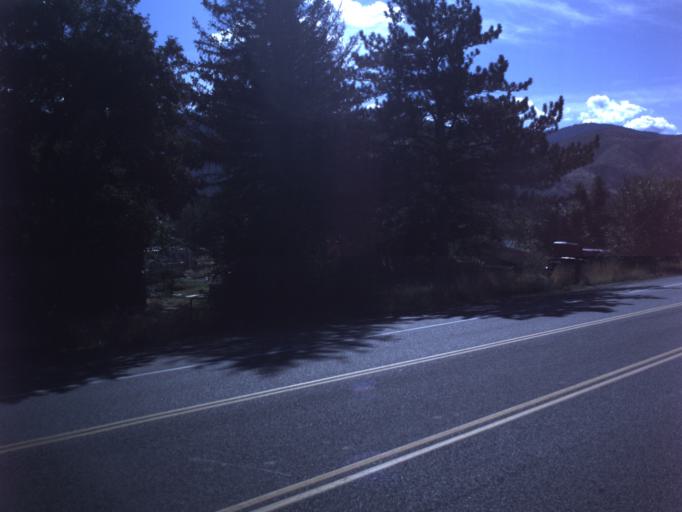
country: US
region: Utah
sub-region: Juab County
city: Nephi
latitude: 39.5529
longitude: -111.8639
